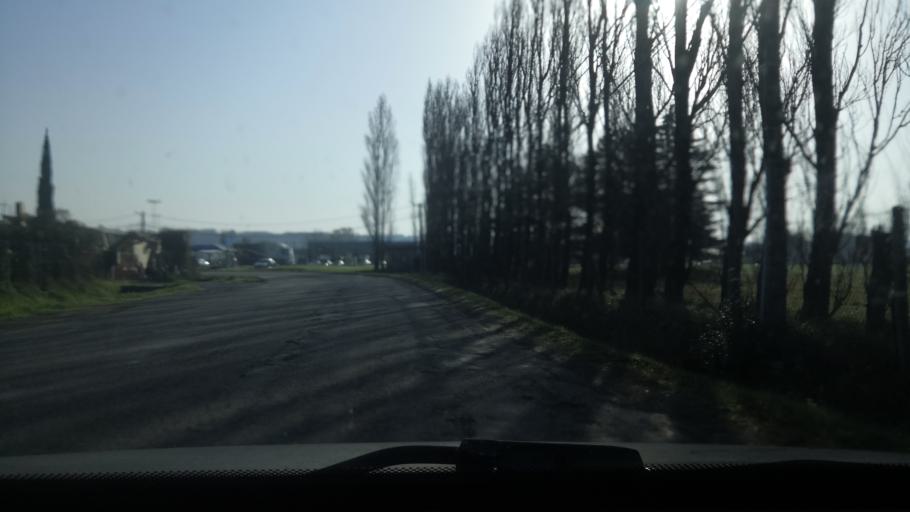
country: FR
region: Rhone-Alpes
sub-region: Departement de la Drome
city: Ancone
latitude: 44.5782
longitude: 4.7421
